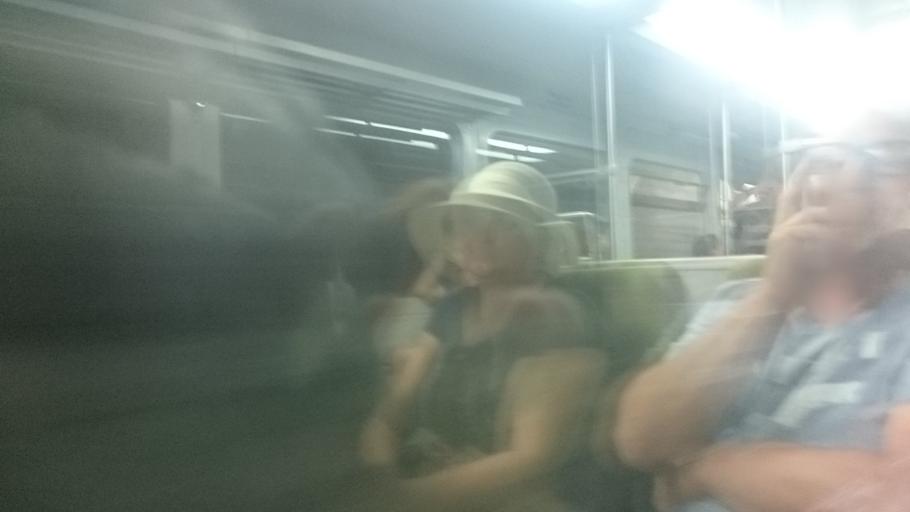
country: ES
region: Catalonia
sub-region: Provincia de Girona
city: Ribes de Freser
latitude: 42.3942
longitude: 2.1538
